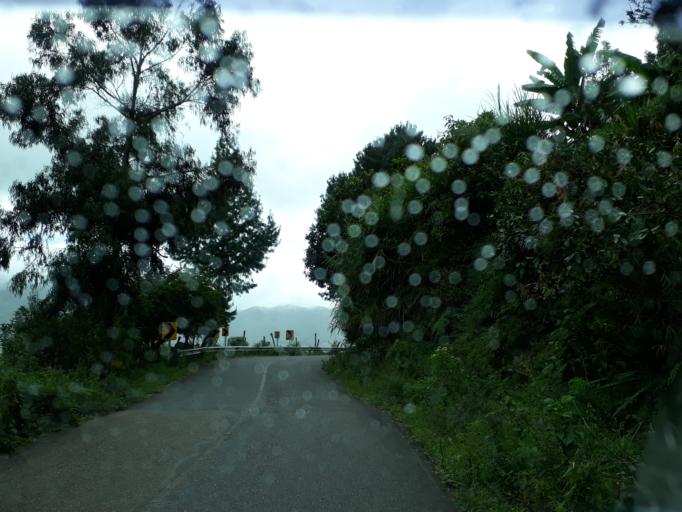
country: CO
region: Cundinamarca
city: Cabrera
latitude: 4.0138
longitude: -74.5080
